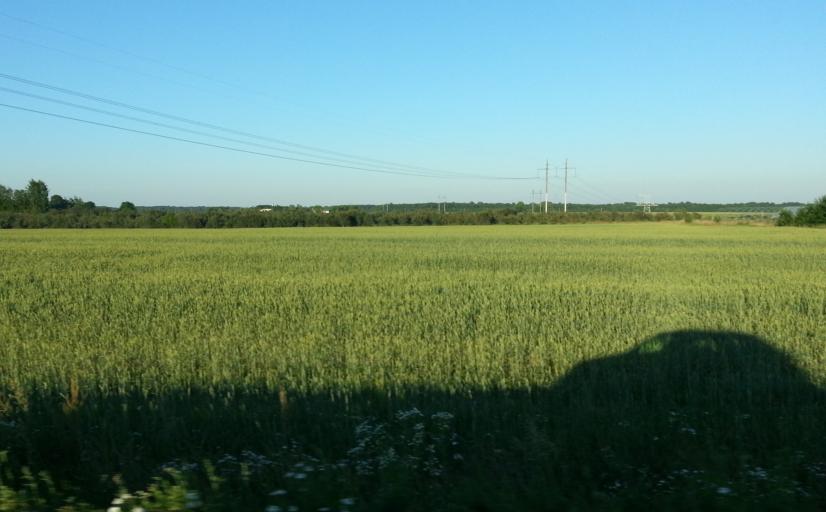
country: LT
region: Panevezys
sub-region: Panevezys City
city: Panevezys
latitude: 55.6341
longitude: 24.3478
